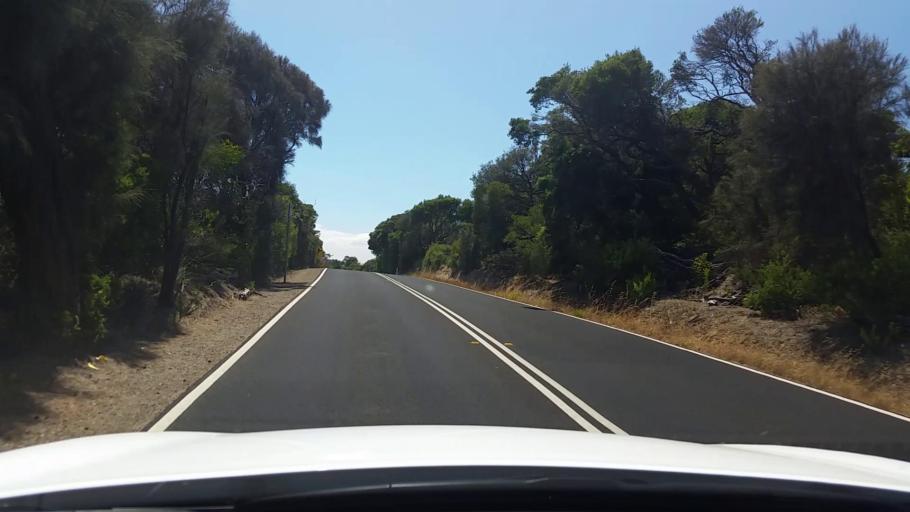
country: AU
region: Victoria
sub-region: Mornington Peninsula
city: Mount Martha
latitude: -38.2794
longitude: 144.9986
